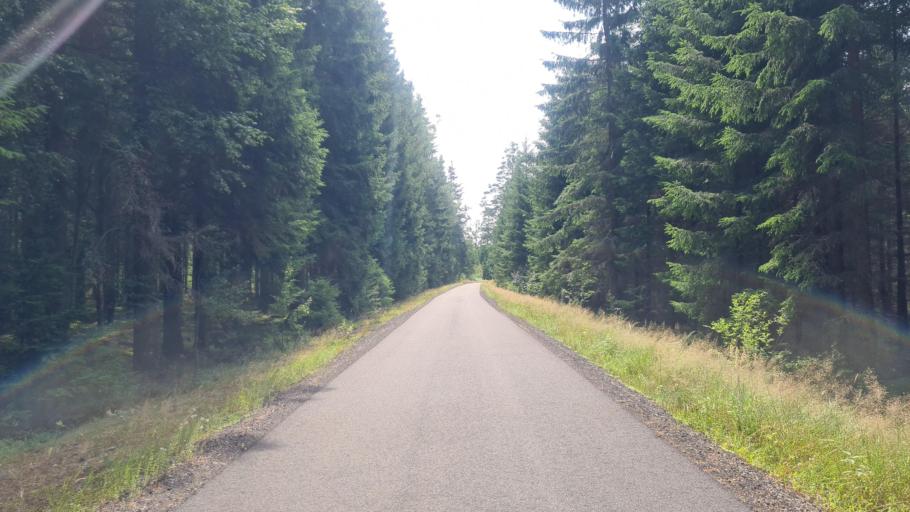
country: SE
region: Kronoberg
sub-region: Ljungby Kommun
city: Ljungby
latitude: 56.8629
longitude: 13.9776
